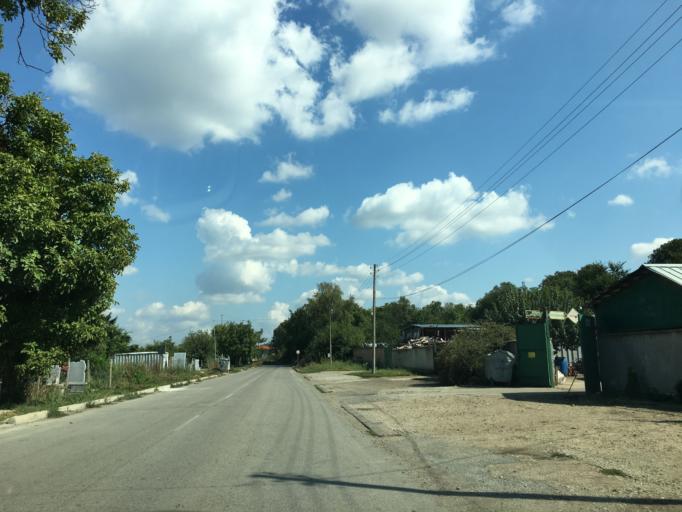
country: BG
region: Montana
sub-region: Obshtina Lom
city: Lom
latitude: 43.8252
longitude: 23.2103
